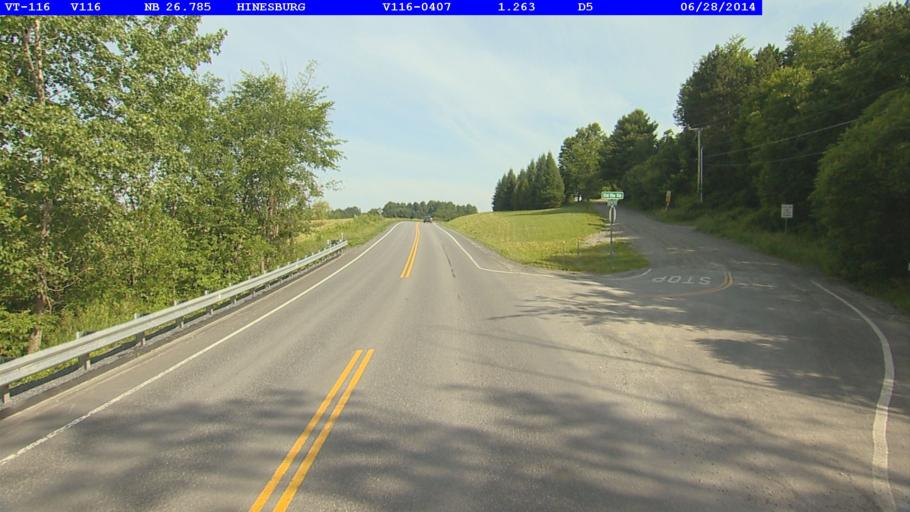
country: US
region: Vermont
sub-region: Chittenden County
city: Hinesburg
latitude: 44.2979
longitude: -73.0728
